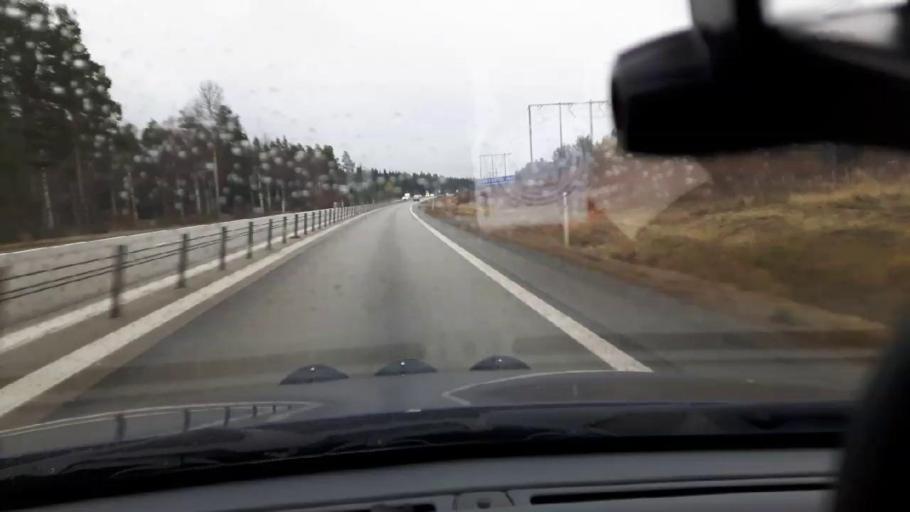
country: SE
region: Jaemtland
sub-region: OEstersunds Kommun
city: Brunflo
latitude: 63.1607
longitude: 14.7533
